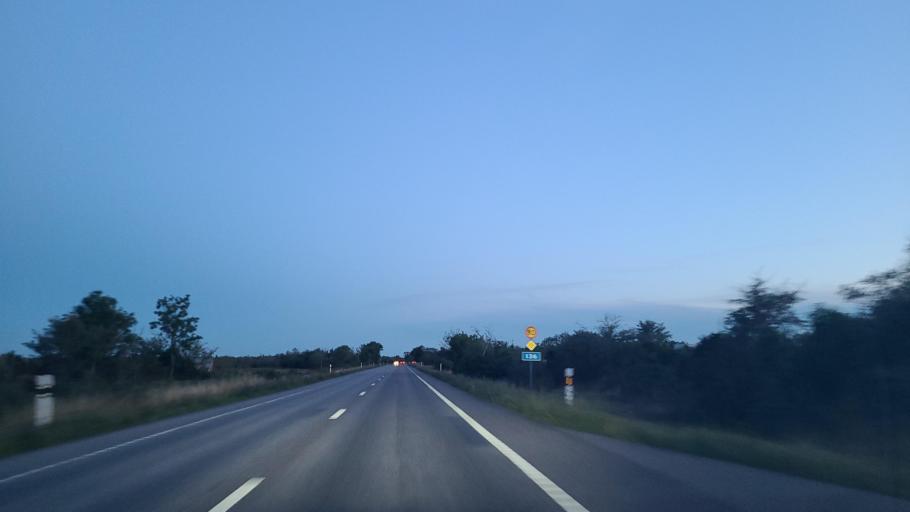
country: SE
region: Kalmar
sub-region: Borgholms Kommun
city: Borgholm
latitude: 56.8134
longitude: 16.5997
